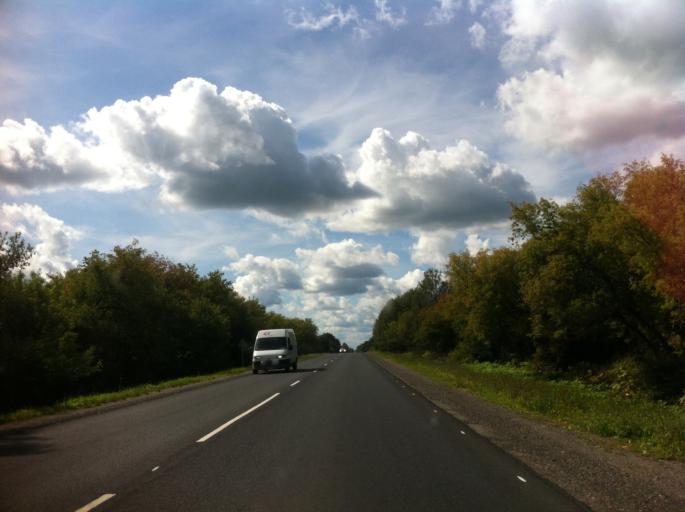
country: RU
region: Pskov
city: Izborsk
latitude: 57.7295
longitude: 27.9686
